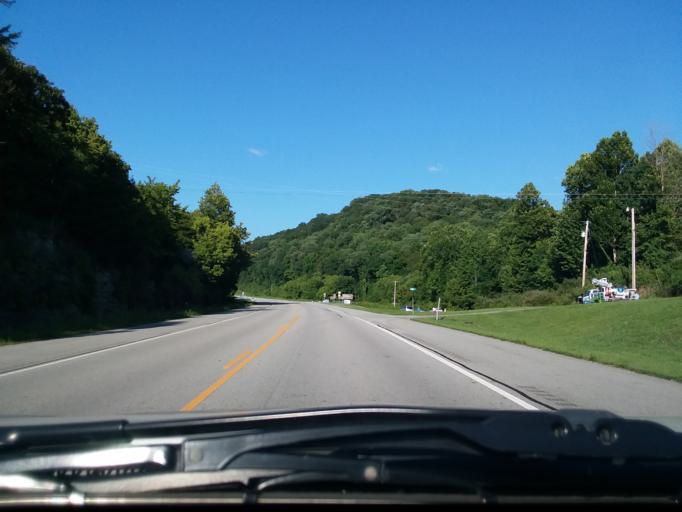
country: US
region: Tennessee
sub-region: Clay County
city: Celina
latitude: 36.5445
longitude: -85.4663
